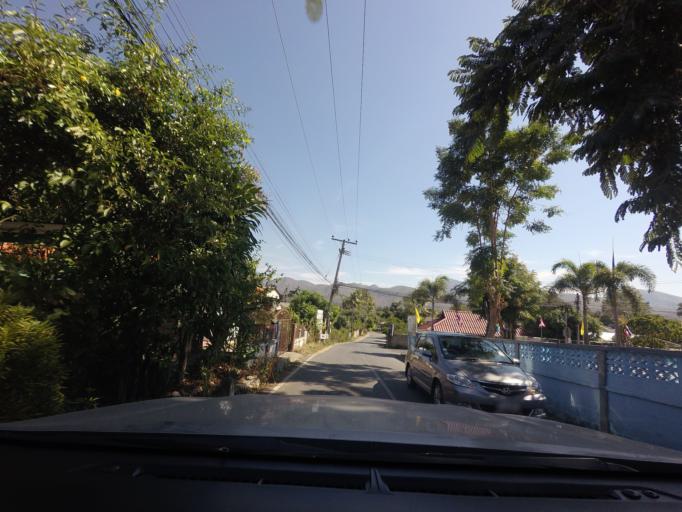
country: TH
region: Mae Hong Son
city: Wiang Nuea
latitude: 19.3860
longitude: 98.4395
